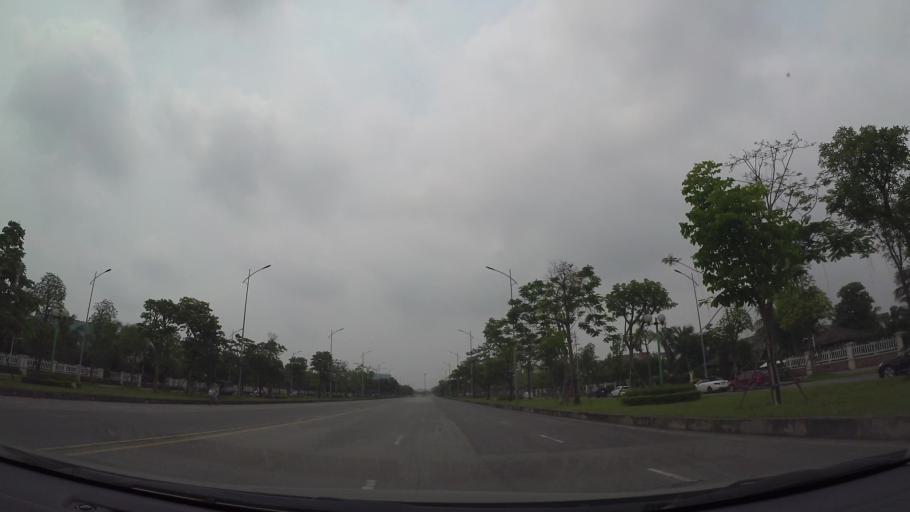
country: VN
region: Ha Noi
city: Trau Quy
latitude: 21.0494
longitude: 105.9151
